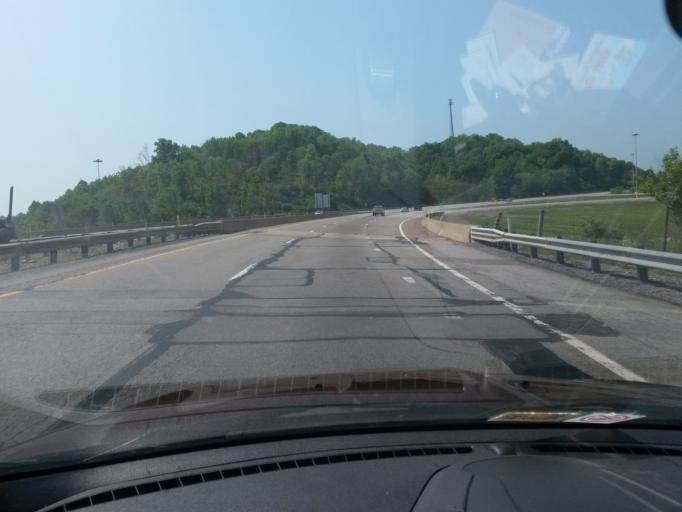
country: US
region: West Virginia
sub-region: Lewis County
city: Weston
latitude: 38.9642
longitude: -80.5152
